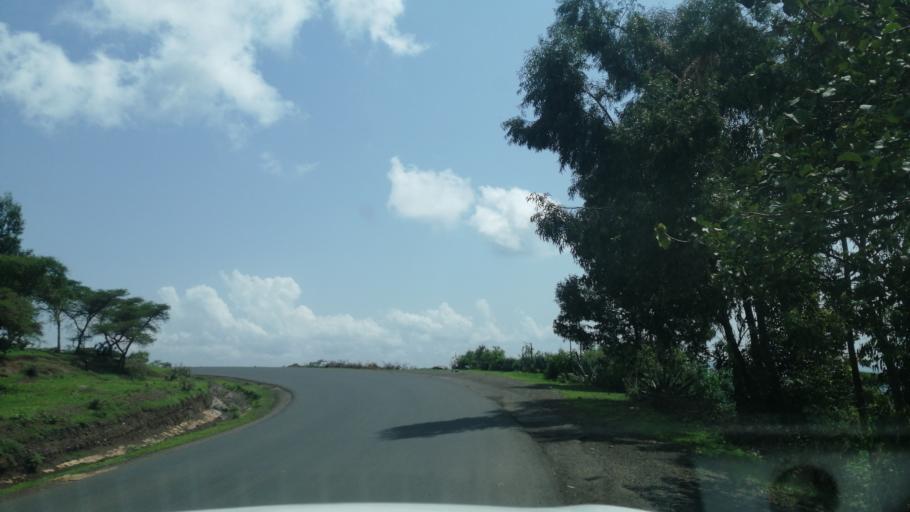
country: ET
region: Oromiya
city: Guder
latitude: 8.9930
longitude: 37.6240
